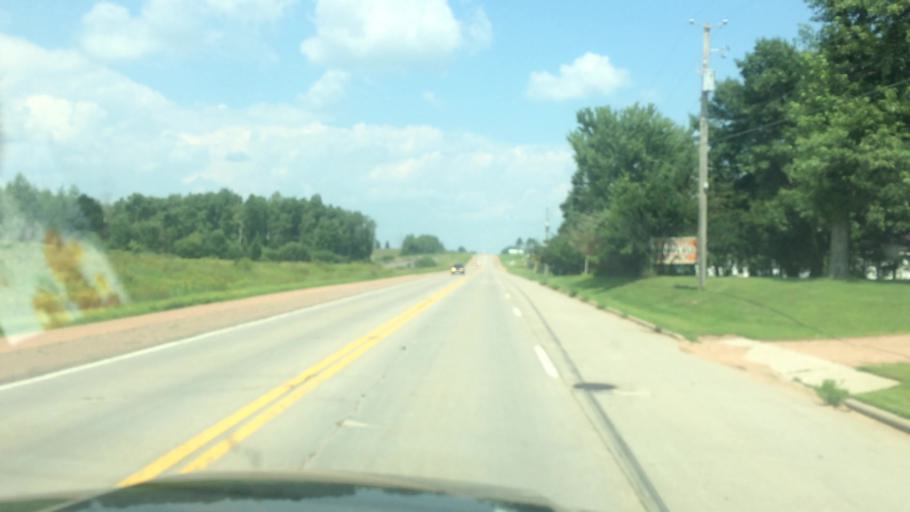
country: US
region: Wisconsin
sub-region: Clark County
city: Colby
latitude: 44.8560
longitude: -90.3159
